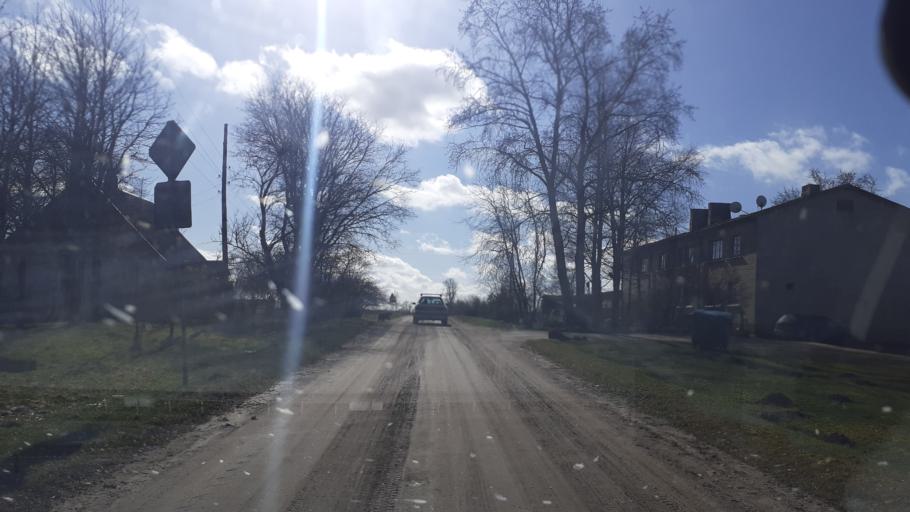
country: LV
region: Kuldigas Rajons
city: Kuldiga
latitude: 56.9338
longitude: 22.1561
